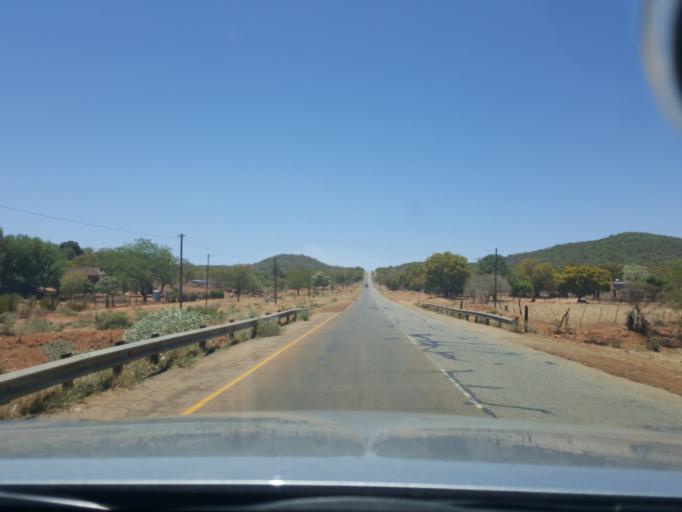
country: BW
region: South East
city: Lobatse
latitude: -25.3051
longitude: 25.9287
